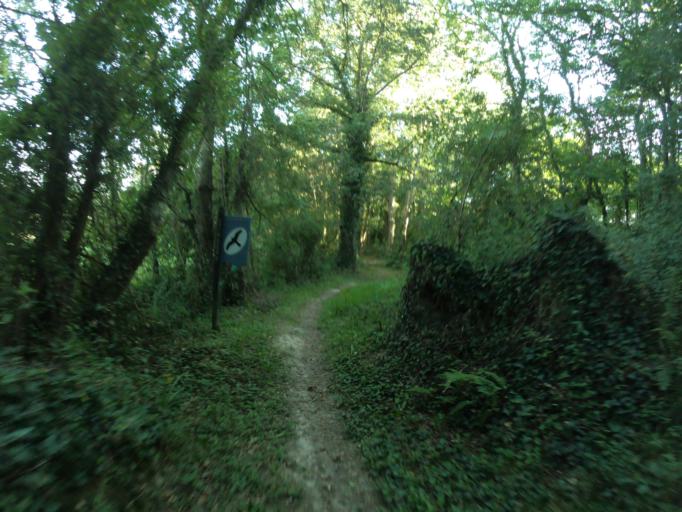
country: FR
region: Midi-Pyrenees
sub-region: Departement de l'Ariege
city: La Tour-du-Crieu
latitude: 43.0990
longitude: 1.7136
